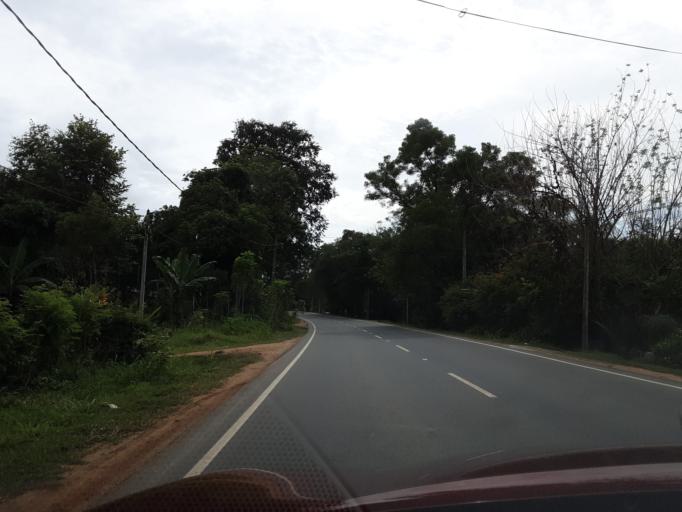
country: LK
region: Eastern Province
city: Eravur Town
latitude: 7.5152
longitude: 81.3415
